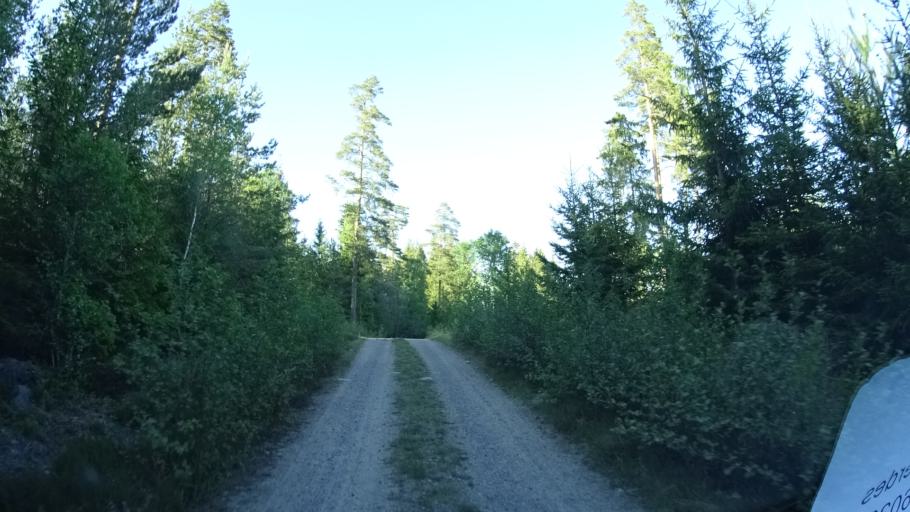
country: SE
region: OEstergoetland
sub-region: Finspangs Kommun
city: Finspang
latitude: 58.6115
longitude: 15.6811
